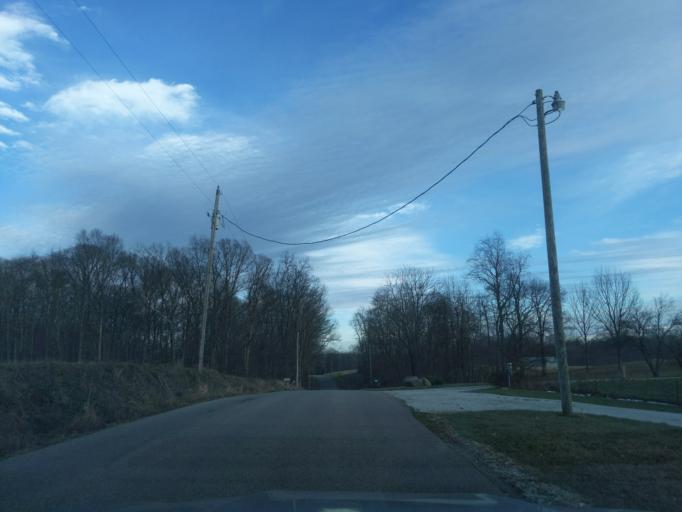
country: US
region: Indiana
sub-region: Decatur County
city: Westport
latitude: 39.2335
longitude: -85.5374
